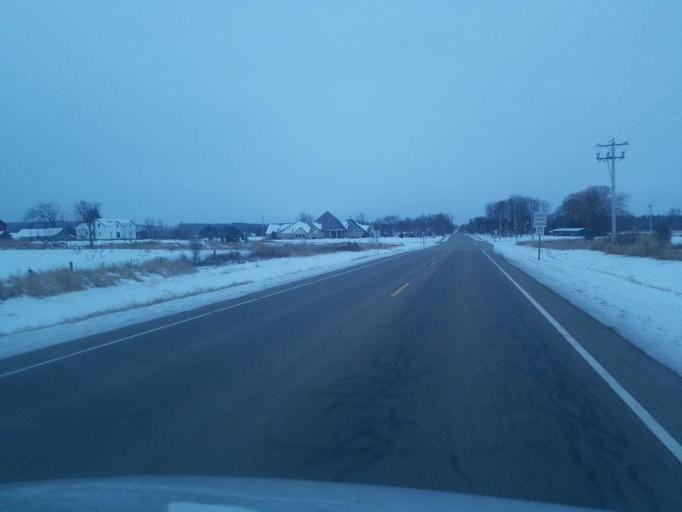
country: US
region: Wisconsin
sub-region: Waupaca County
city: Manawa
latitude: 44.4773
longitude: -88.9204
